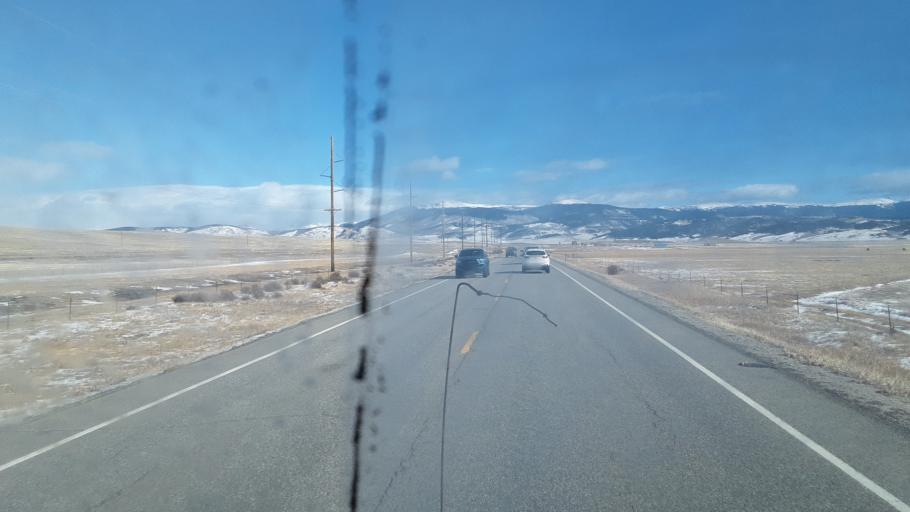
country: US
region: Colorado
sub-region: Park County
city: Fairplay
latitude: 39.3519
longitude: -105.8297
